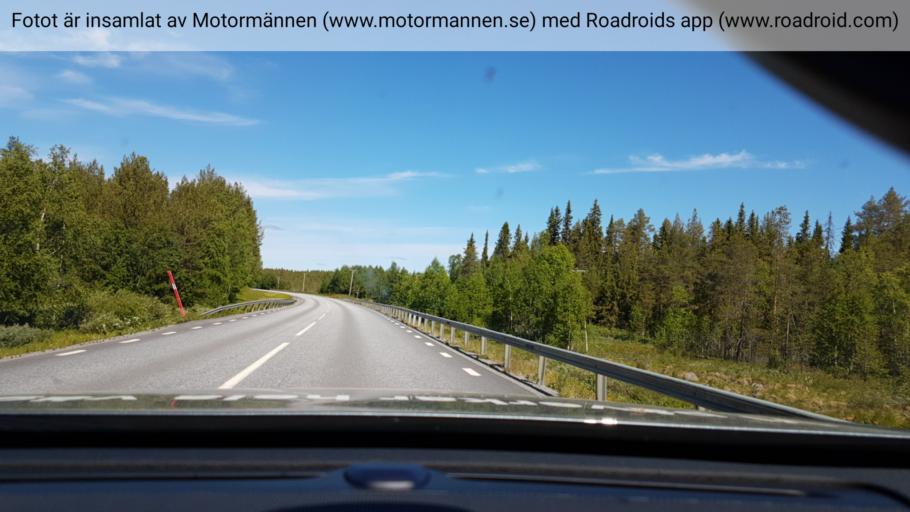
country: SE
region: Vaesterbotten
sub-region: Vilhelmina Kommun
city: Vilhelmina
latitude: 64.5235
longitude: 16.7626
